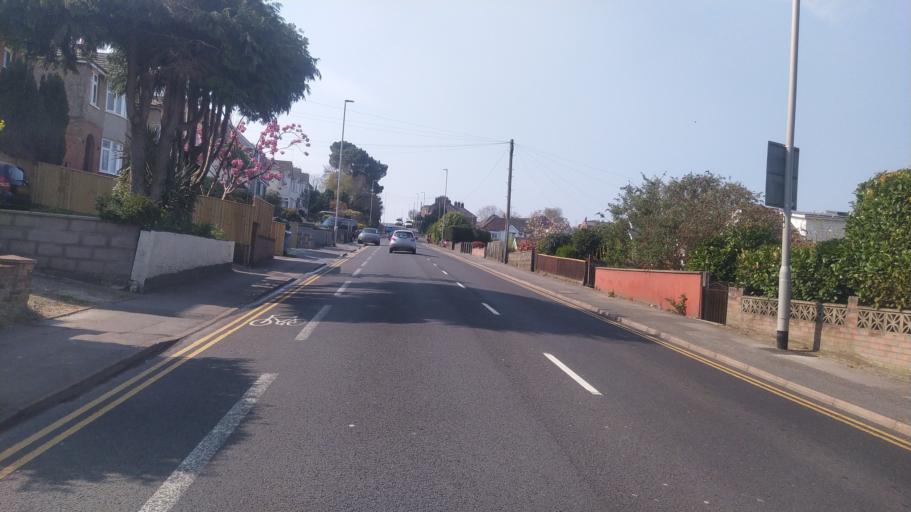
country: GB
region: England
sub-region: Dorset
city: Parkstone
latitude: 50.7308
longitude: -1.9230
